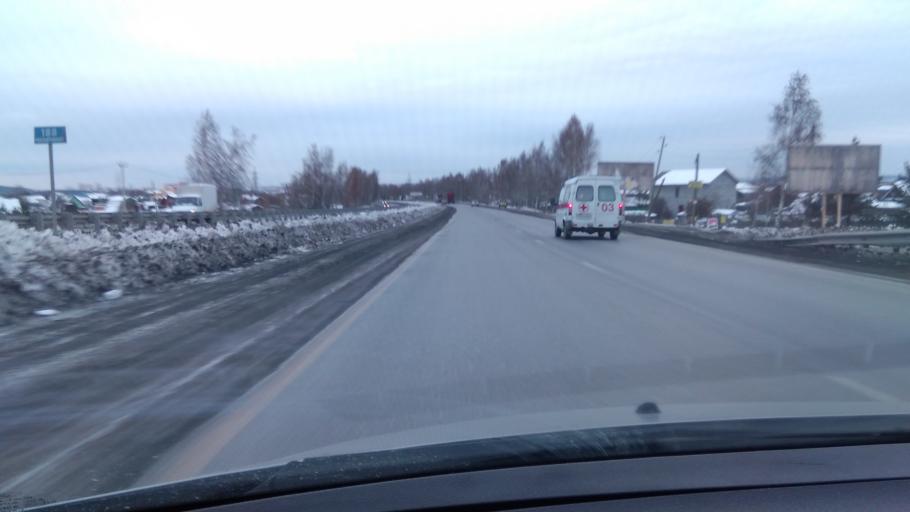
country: RU
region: Sverdlovsk
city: Aramil
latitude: 56.6984
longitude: 60.7500
